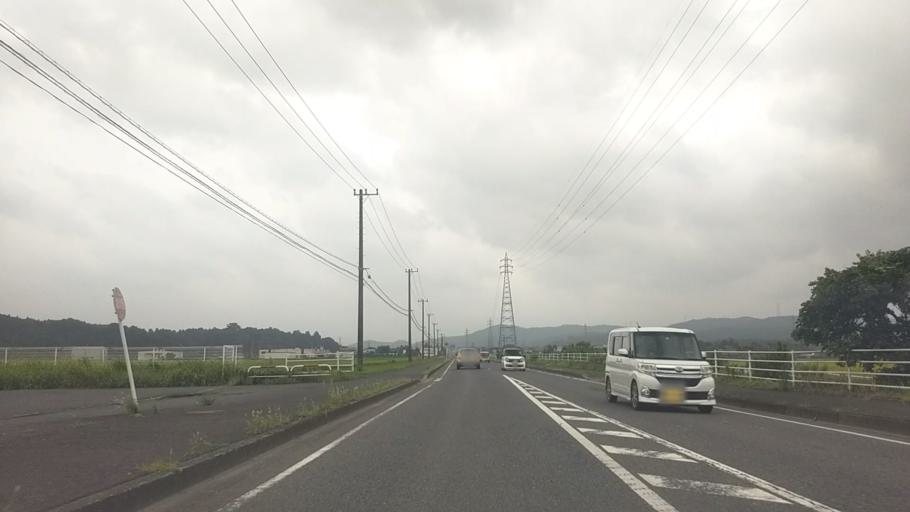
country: JP
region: Chiba
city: Kisarazu
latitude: 35.3296
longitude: 140.0550
